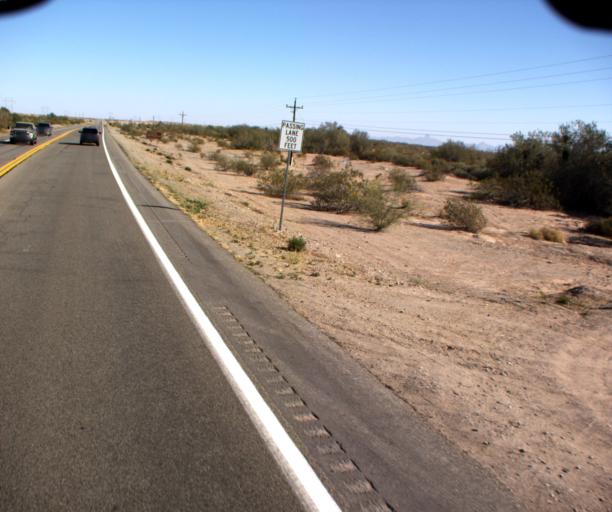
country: US
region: Arizona
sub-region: Yuma County
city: Fortuna Foothills
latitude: 32.7933
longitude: -114.3814
